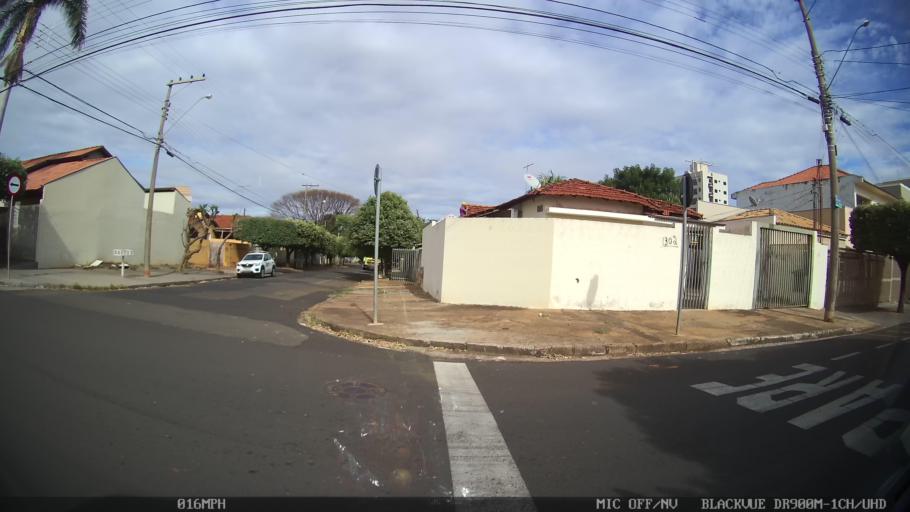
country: BR
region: Sao Paulo
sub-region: Sao Jose Do Rio Preto
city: Sao Jose do Rio Preto
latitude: -20.8345
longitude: -49.3803
